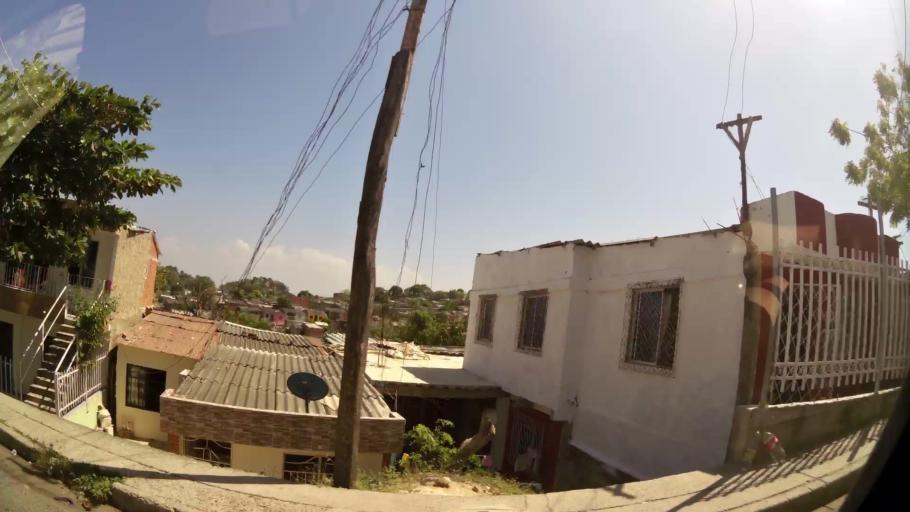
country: CO
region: Bolivar
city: Cartagena
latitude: 10.4339
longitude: -75.5252
